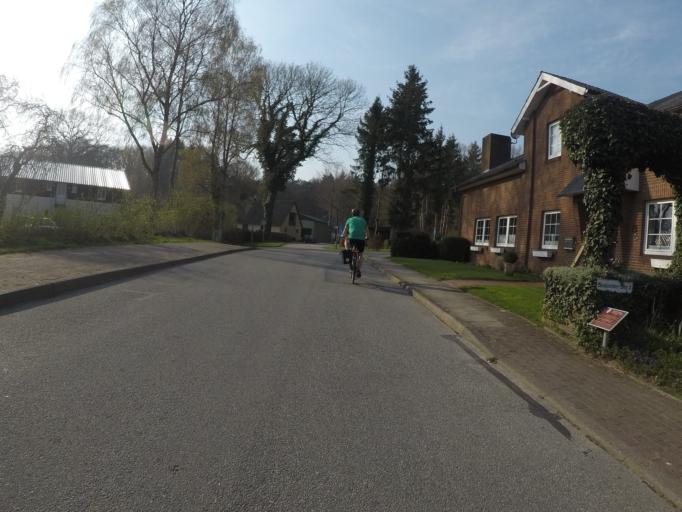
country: DE
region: Schleswig-Holstein
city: Wittenborn
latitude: 53.9267
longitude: 10.2230
